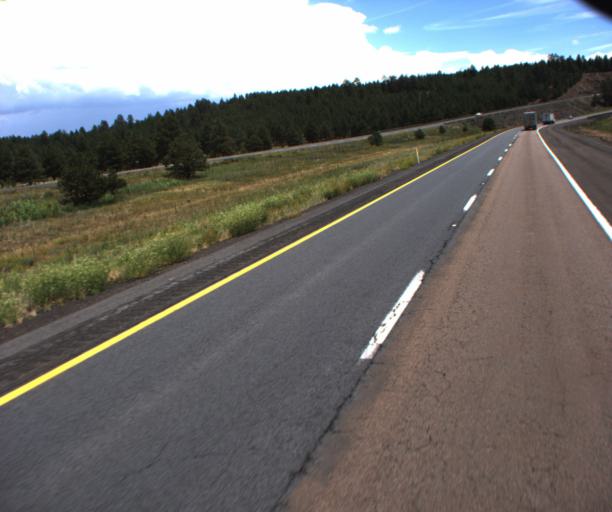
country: US
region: Arizona
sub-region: Coconino County
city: Flagstaff
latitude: 35.2133
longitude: -111.7784
